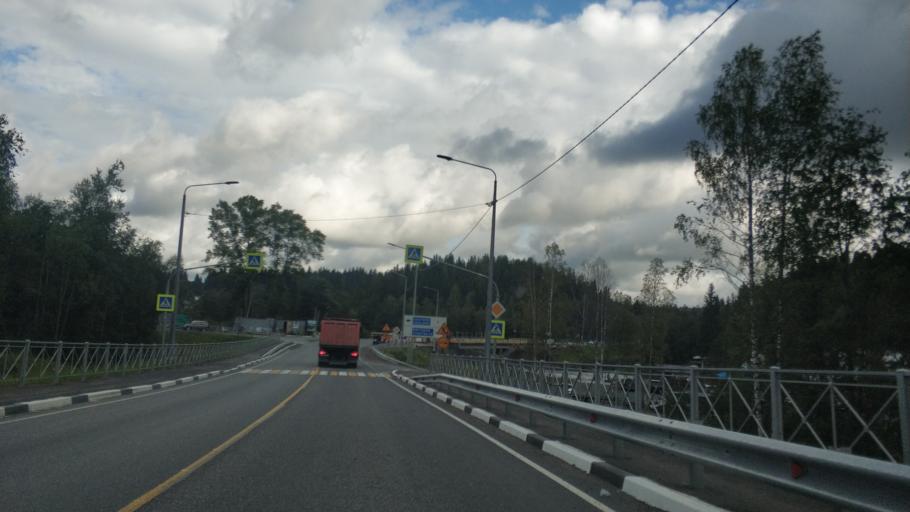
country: RU
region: Republic of Karelia
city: Ruskeala
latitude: 61.9361
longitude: 30.5907
